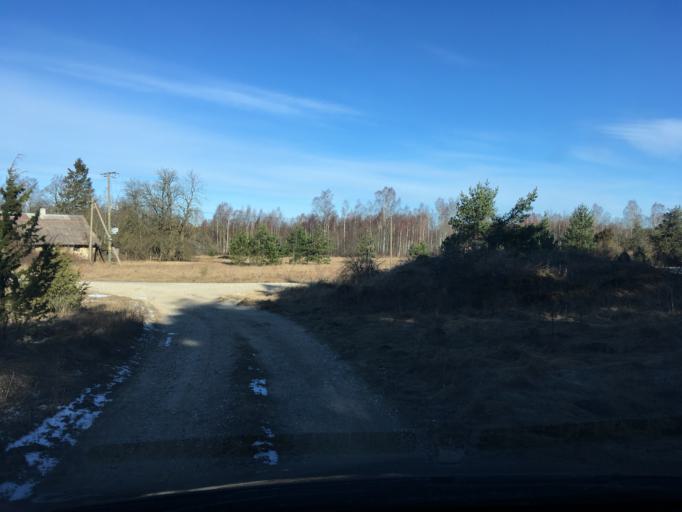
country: EE
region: Laeaene
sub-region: Lihula vald
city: Lihula
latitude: 58.5855
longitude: 23.7133
